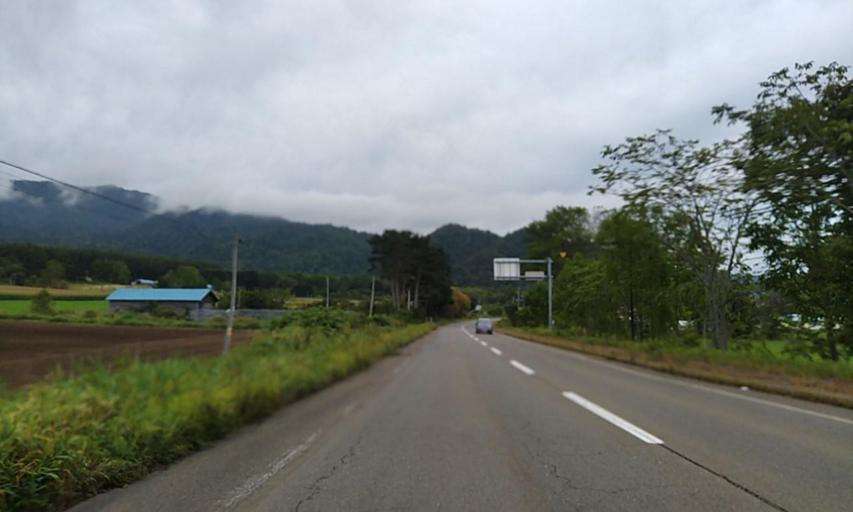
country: JP
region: Hokkaido
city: Bihoro
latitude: 43.5812
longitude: 144.2778
